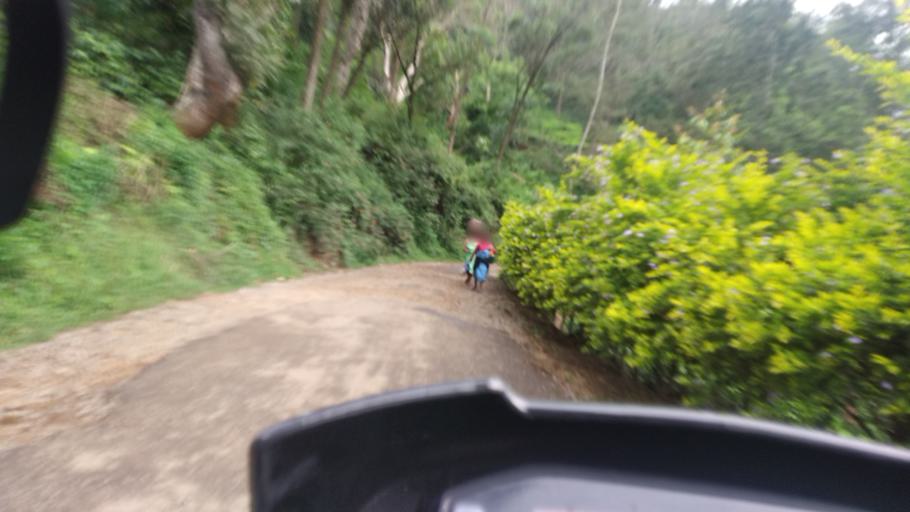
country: IN
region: Tamil Nadu
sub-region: Theni
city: Gudalur
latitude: 9.5554
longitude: 77.0634
